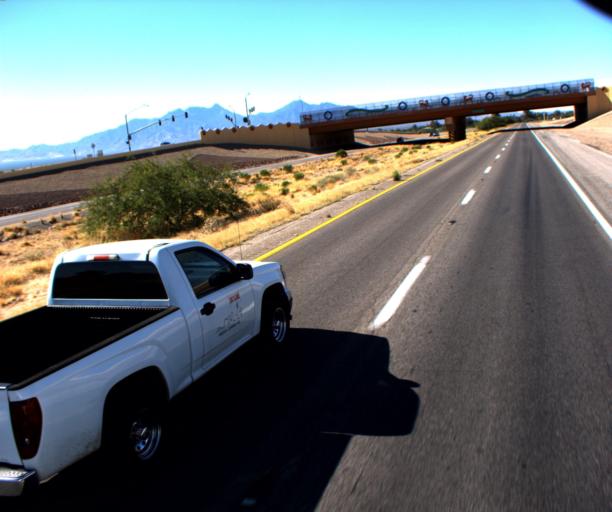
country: US
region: Arizona
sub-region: Pima County
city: Green Valley
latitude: 31.9075
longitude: -110.9858
